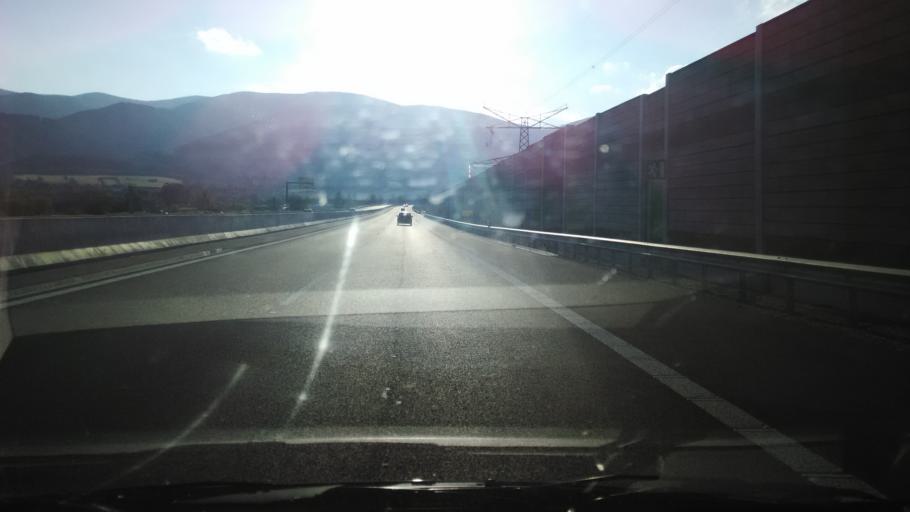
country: SK
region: Zilinsky
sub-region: Okres Zilina
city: Vrutky
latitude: 49.1216
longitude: 18.9313
